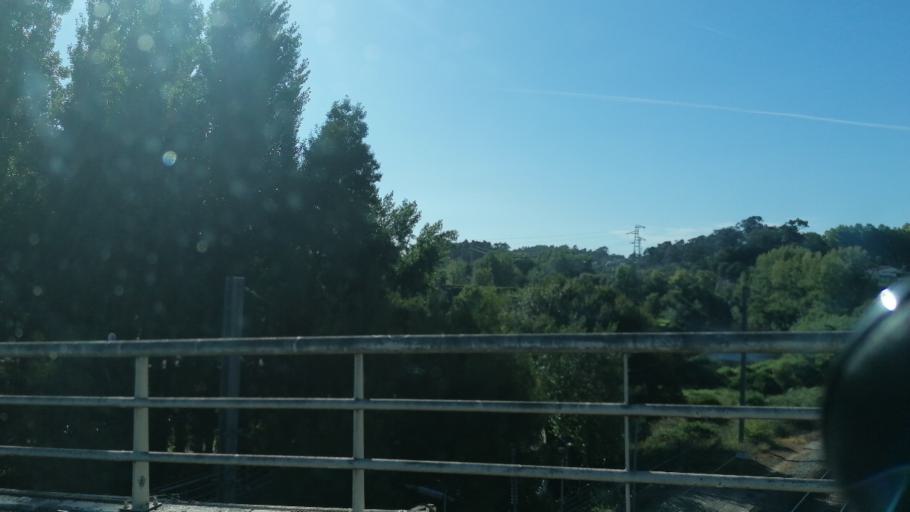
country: PT
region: Porto
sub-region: Santo Tirso
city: Santo Tirso
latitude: 41.3513
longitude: -8.4736
